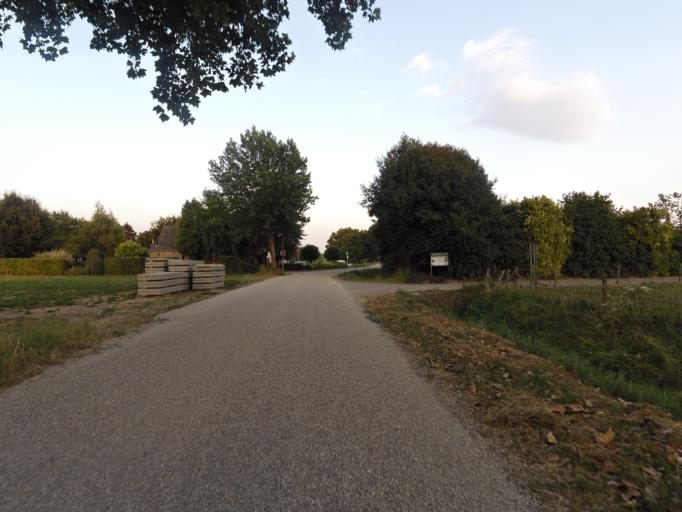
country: NL
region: Gelderland
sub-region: Gemeente Zevenaar
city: Zevenaar
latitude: 51.8844
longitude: 6.0704
